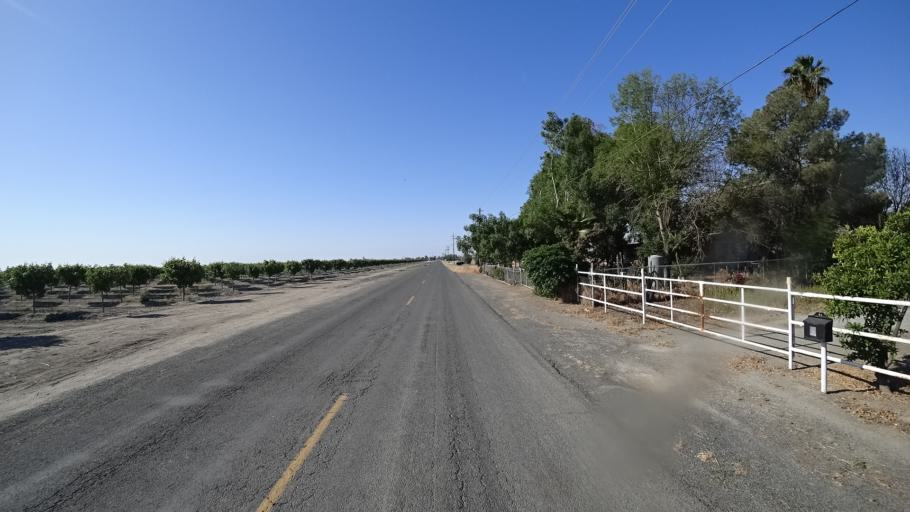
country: US
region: California
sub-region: Kings County
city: Corcoran
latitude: 36.1322
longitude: -119.5633
